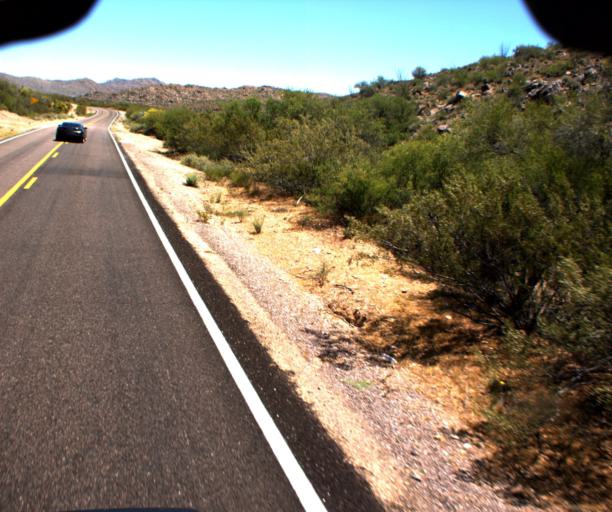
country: US
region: Arizona
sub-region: Yavapai County
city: Bagdad
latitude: 34.4802
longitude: -113.2000
